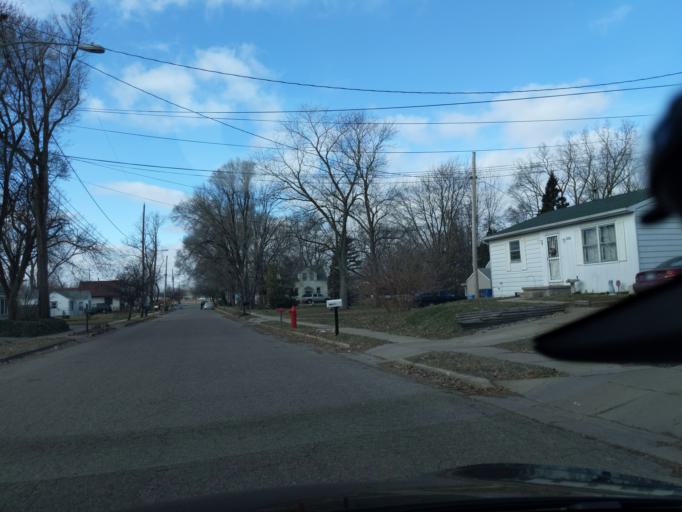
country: US
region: Michigan
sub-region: Ingham County
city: Lansing
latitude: 42.6718
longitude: -84.5842
